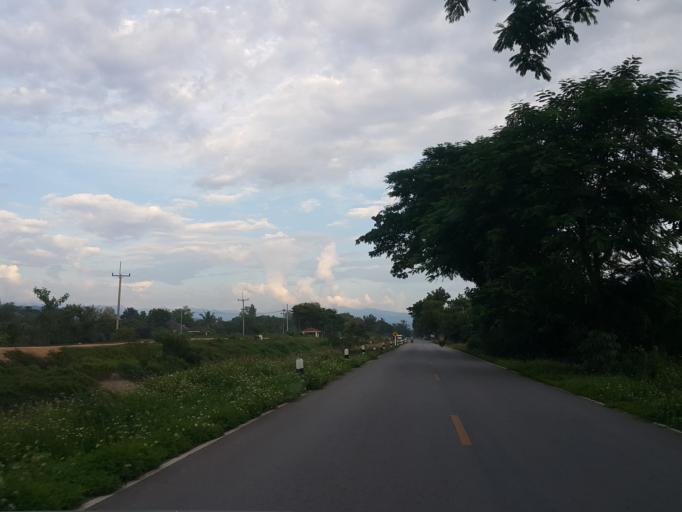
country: TH
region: Chiang Mai
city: San Sai
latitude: 18.8927
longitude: 99.0702
